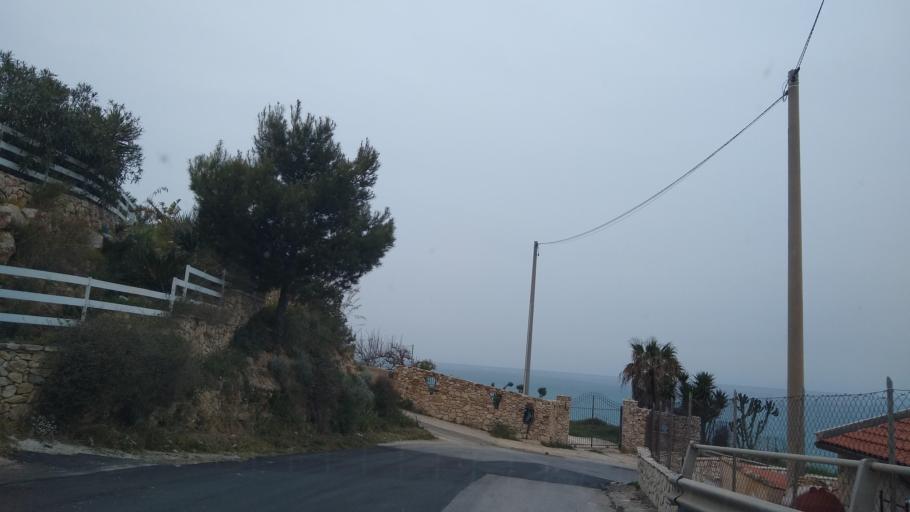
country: IT
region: Sicily
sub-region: Trapani
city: Castellammare del Golfo
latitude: 38.0218
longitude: 12.8969
